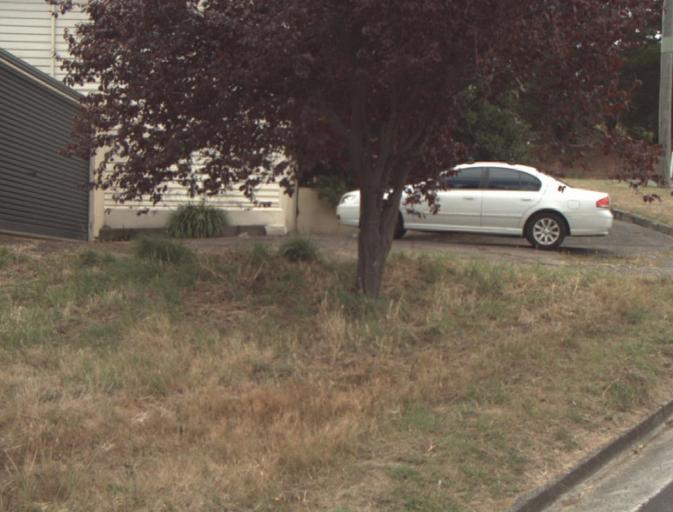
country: AU
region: Tasmania
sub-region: Launceston
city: East Launceston
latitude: -41.4533
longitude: 147.1507
